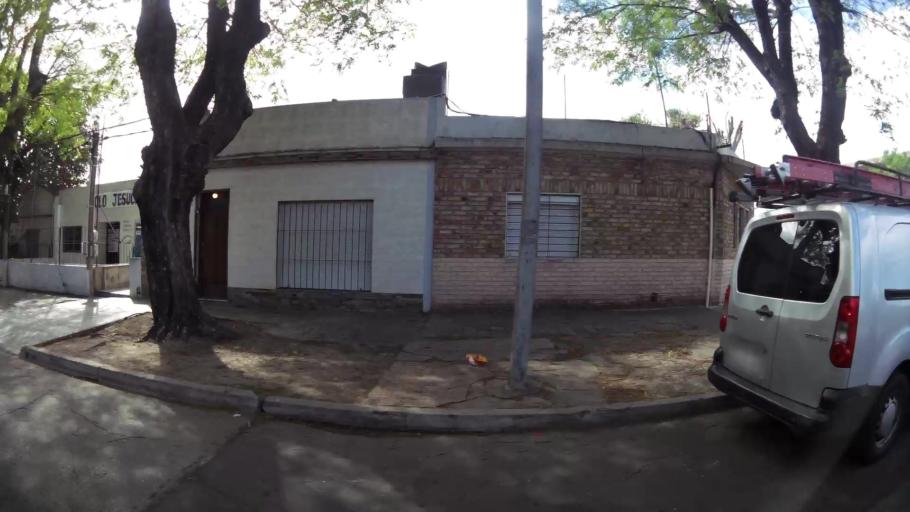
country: UY
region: Montevideo
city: Montevideo
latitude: -34.8673
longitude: -56.1559
